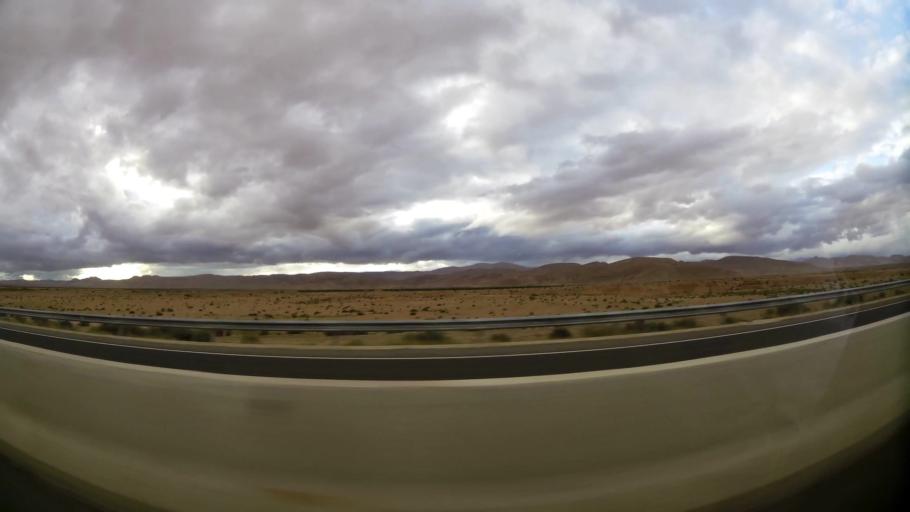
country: MA
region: Taza-Al Hoceima-Taounate
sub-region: Taza
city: Guercif
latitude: 34.3233
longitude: -3.5716
